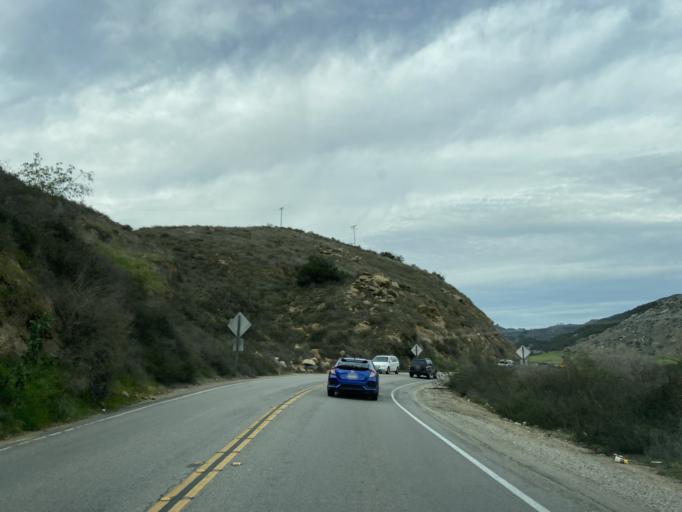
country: US
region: California
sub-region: San Diego County
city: Rainbow
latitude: 33.3398
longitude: -117.1334
